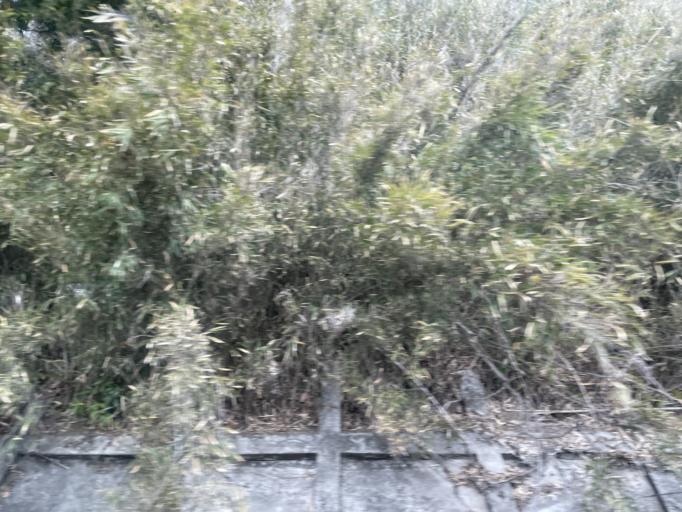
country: JP
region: Chiba
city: Narita
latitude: 35.8276
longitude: 140.2587
